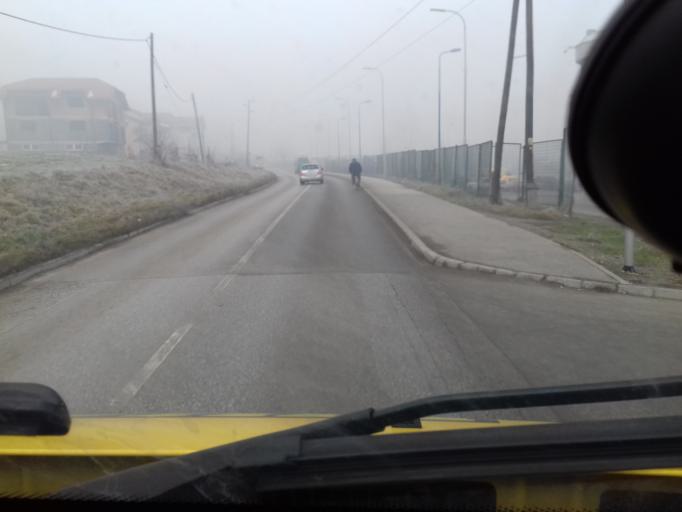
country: BA
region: Federation of Bosnia and Herzegovina
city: Visoko
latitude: 43.9998
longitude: 18.1623
